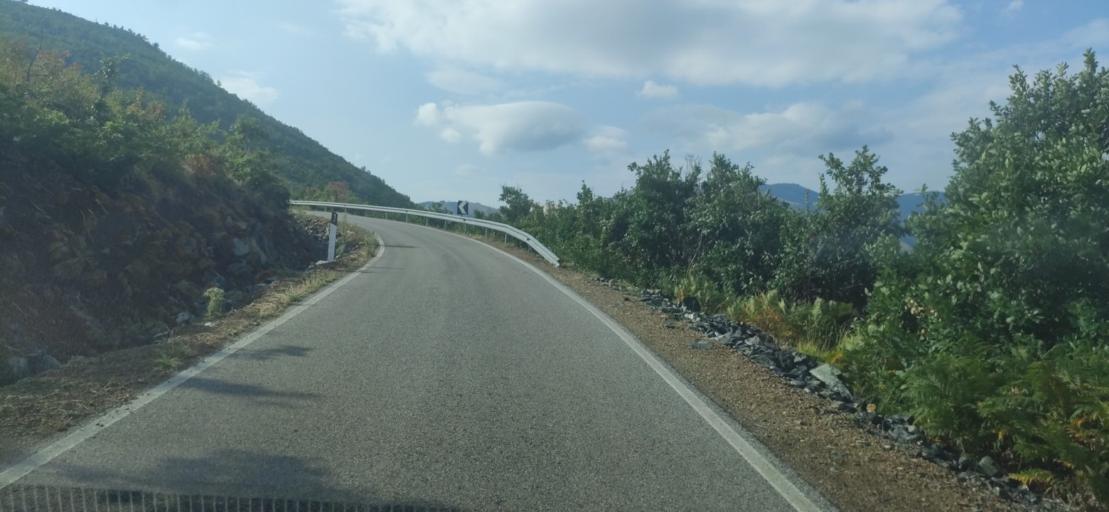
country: AL
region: Shkoder
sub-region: Rrethi i Pukes
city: Iballe
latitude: 42.1723
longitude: 20.0006
